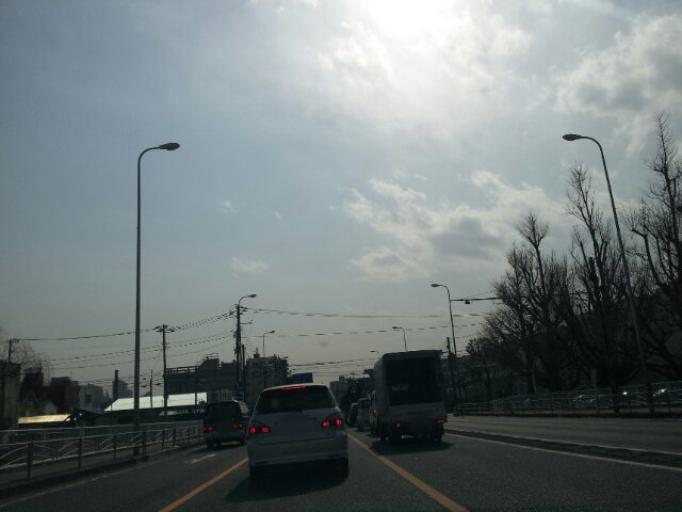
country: JP
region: Kanagawa
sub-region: Kawasaki-shi
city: Kawasaki
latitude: 35.5522
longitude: 139.6948
